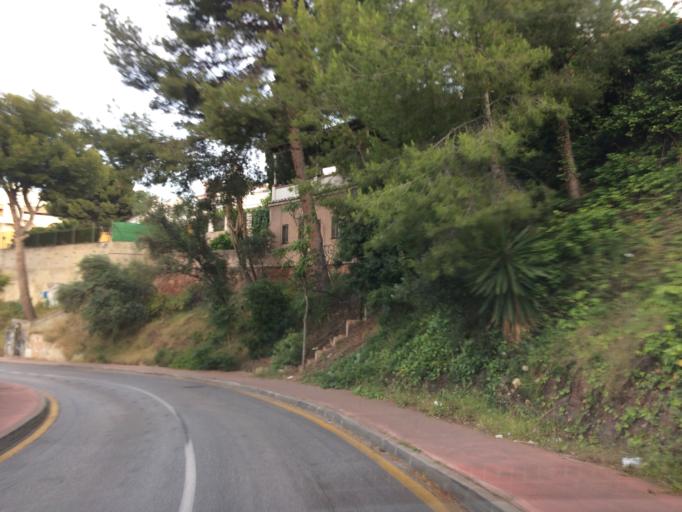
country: ES
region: Andalusia
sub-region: Provincia de Malaga
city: Malaga
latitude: 36.7260
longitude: -4.3847
